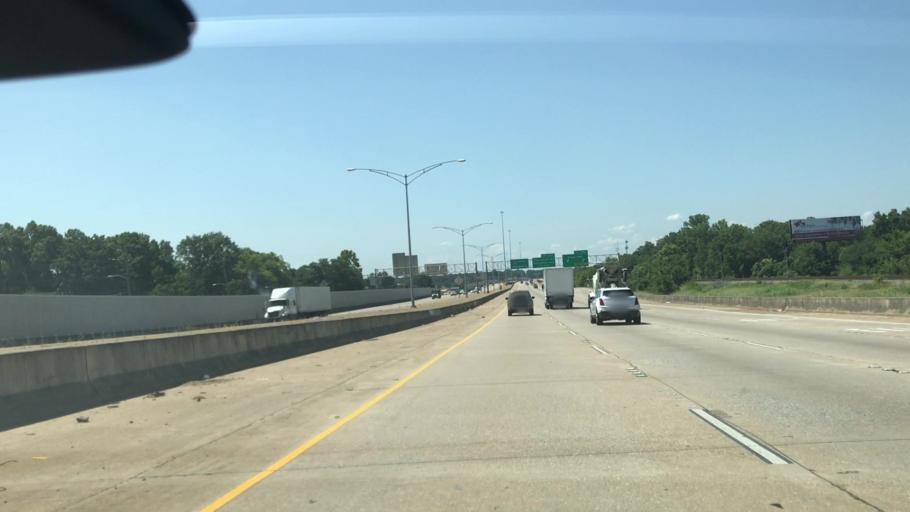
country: US
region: Louisiana
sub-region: Bossier Parish
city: Bossier City
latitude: 32.4880
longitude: -93.7552
